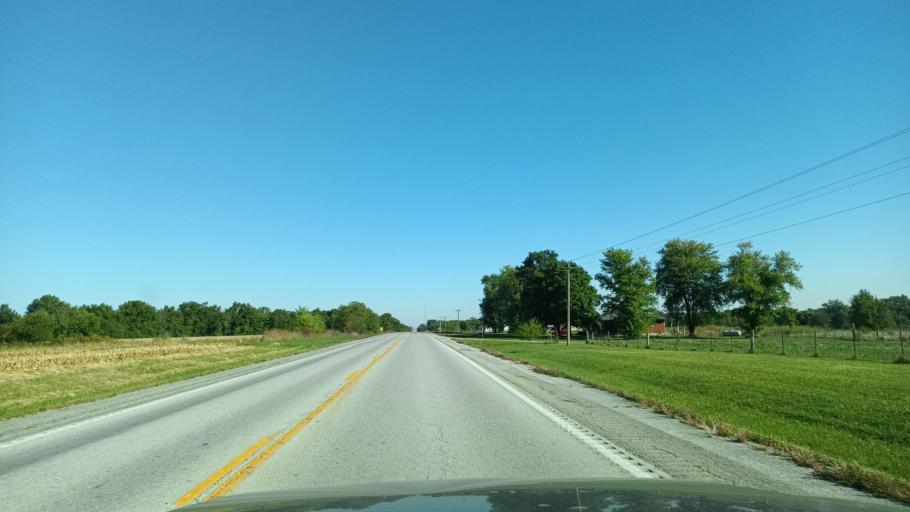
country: US
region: Missouri
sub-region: Audrain County
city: Vandalia
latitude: 39.3815
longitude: -91.6419
